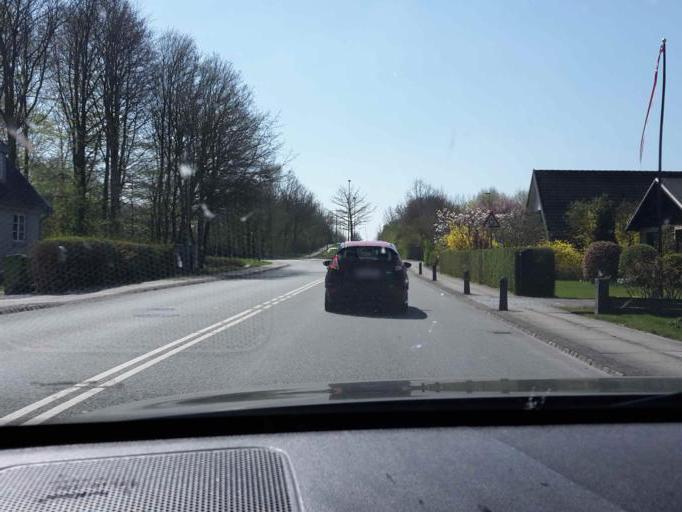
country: DK
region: South Denmark
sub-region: Odense Kommune
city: Bellinge
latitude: 55.3660
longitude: 10.3282
